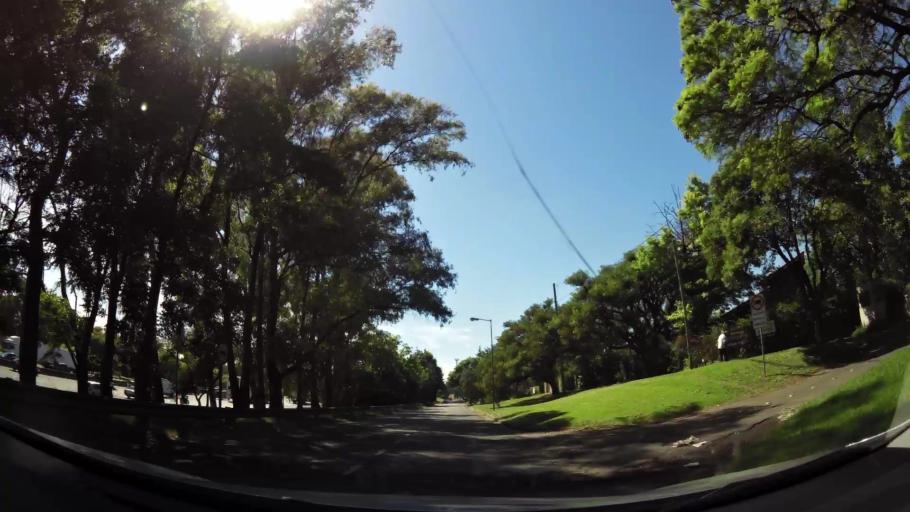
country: AR
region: Buenos Aires
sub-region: Partido de San Isidro
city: San Isidro
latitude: -34.4934
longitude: -58.5612
